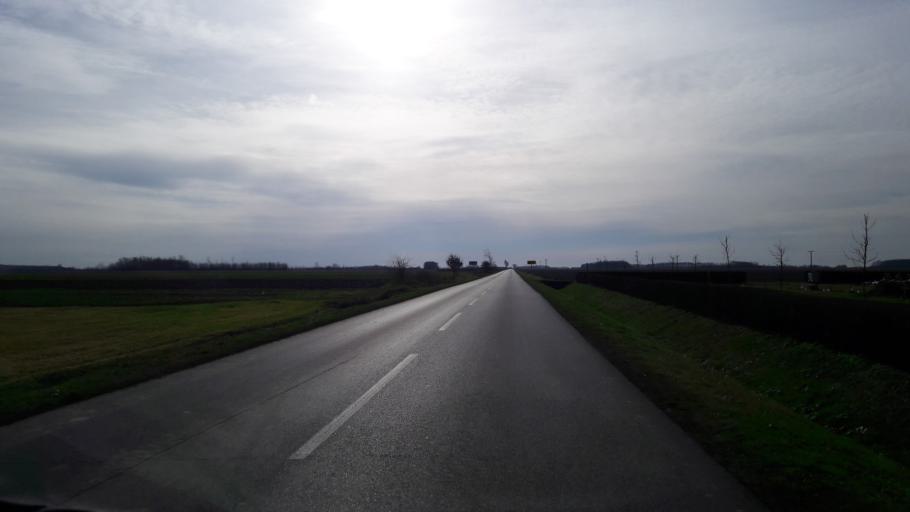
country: HR
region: Osjecko-Baranjska
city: Semeljci
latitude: 45.3423
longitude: 18.5575
